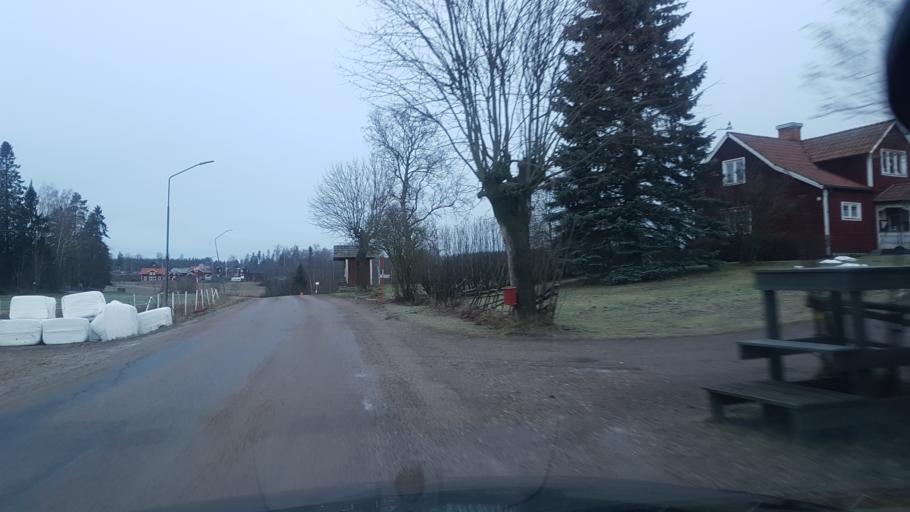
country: SE
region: Dalarna
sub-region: Borlange Kommun
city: Ornas
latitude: 60.4449
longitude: 15.6407
